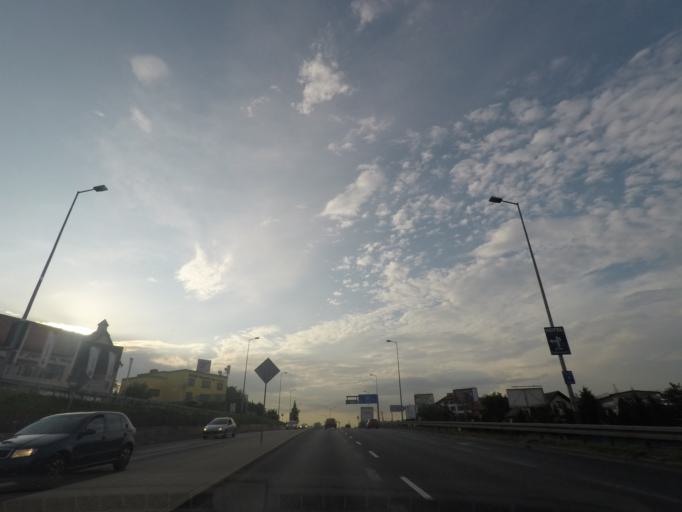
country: PL
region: Lesser Poland Voivodeship
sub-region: Powiat wielicki
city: Wieliczka
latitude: 50.0022
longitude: 20.0251
